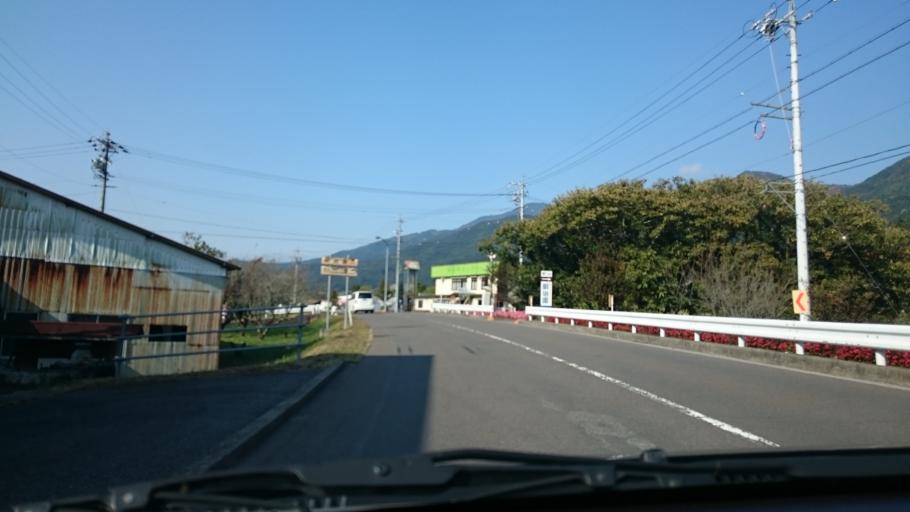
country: JP
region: Gifu
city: Nakatsugawa
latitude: 35.6993
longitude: 137.3808
